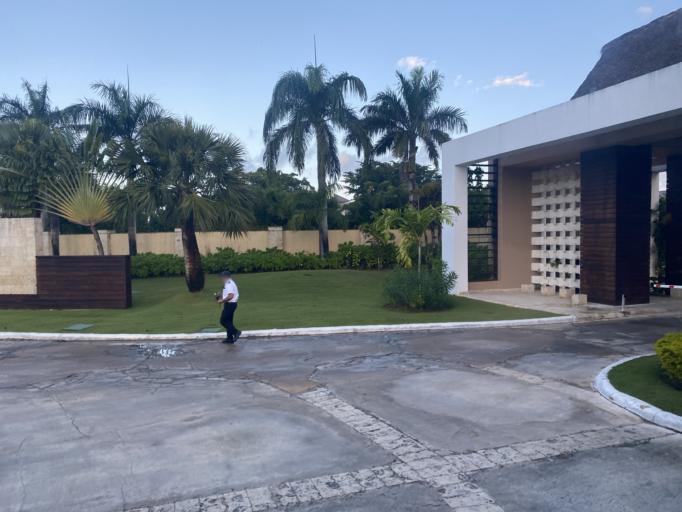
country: DO
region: San Juan
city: Punta Cana
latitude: 18.7255
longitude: -68.4716
